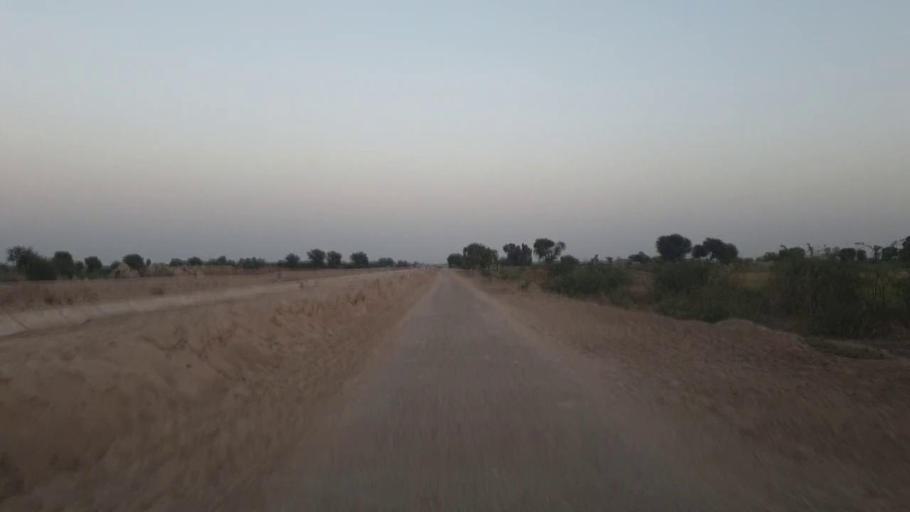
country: PK
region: Sindh
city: Umarkot
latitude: 25.4124
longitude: 69.6788
